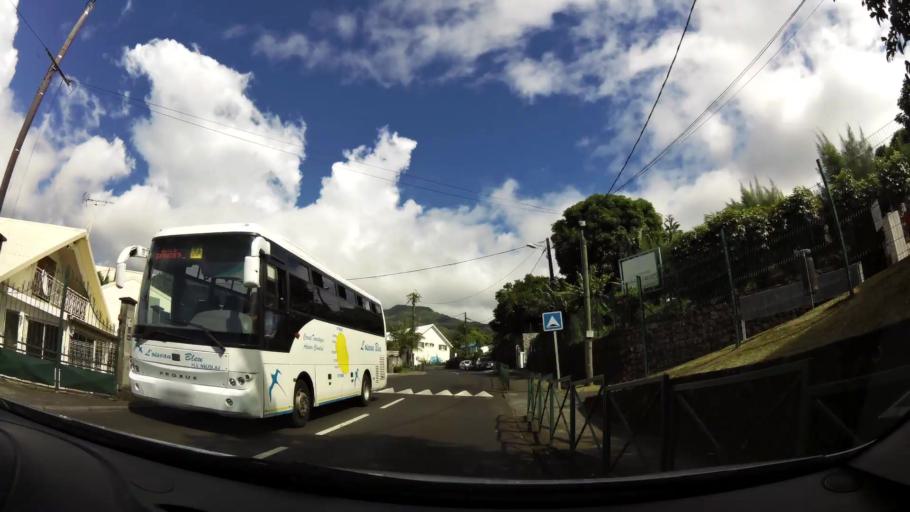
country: RE
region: Reunion
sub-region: Reunion
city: Saint-Denis
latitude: -20.9258
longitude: 55.4940
